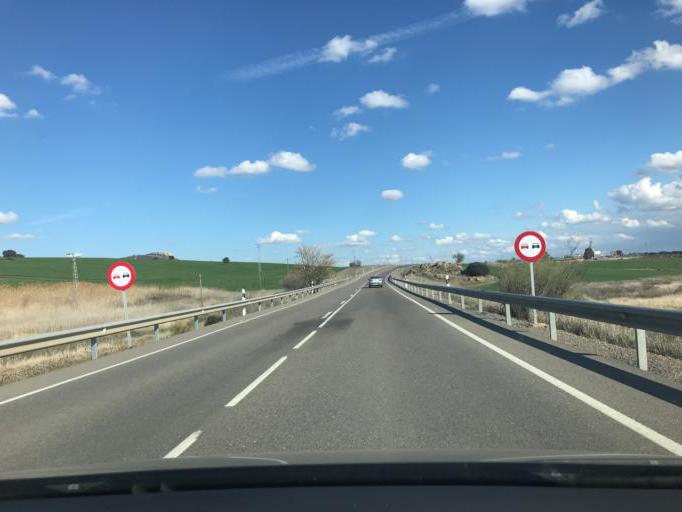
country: ES
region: Andalusia
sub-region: Province of Cordoba
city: Penarroya-Pueblonuevo
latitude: 38.3019
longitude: -5.3291
